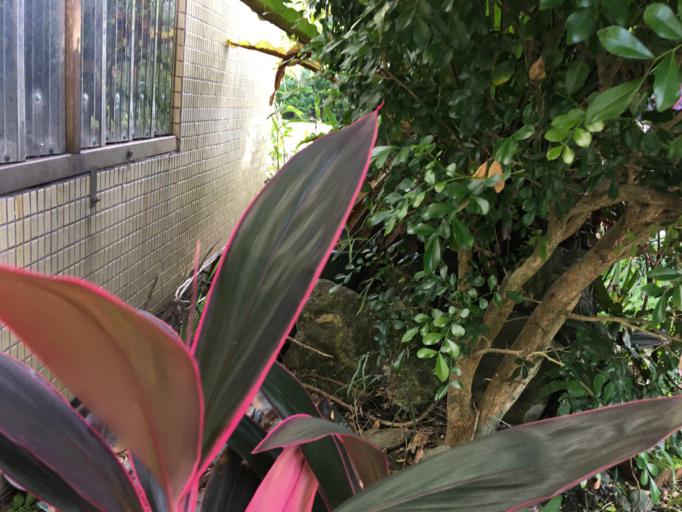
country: TW
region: Taiwan
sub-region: Keelung
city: Keelung
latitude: 24.9667
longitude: 121.9224
